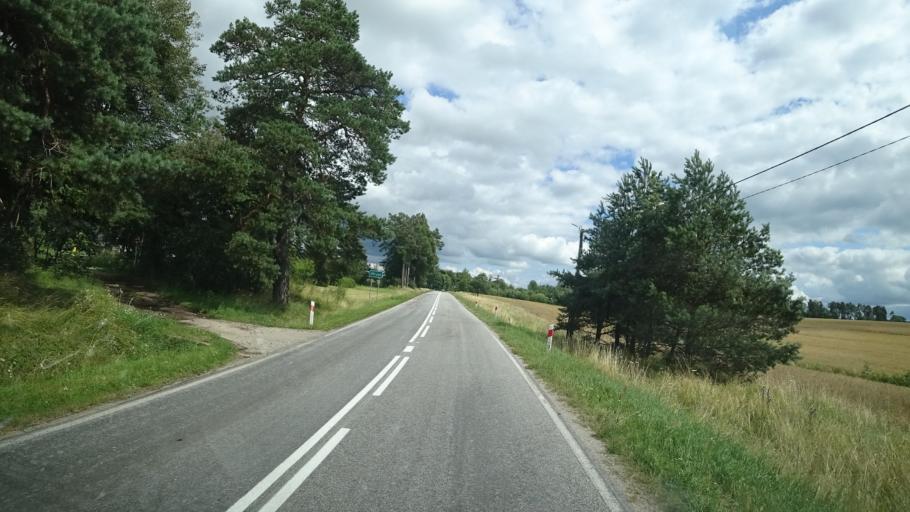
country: PL
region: Warmian-Masurian Voivodeship
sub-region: Powiat goldapski
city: Banie Mazurskie
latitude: 54.2126
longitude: 22.1695
